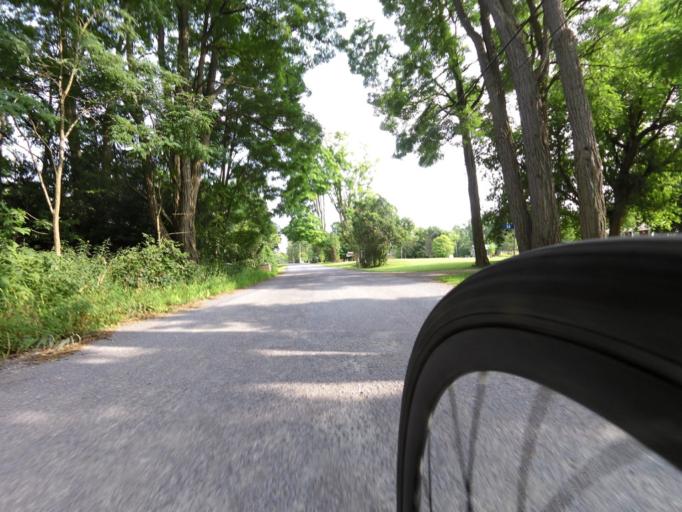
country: CA
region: Ontario
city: Quinte West
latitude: 44.0496
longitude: -77.6296
